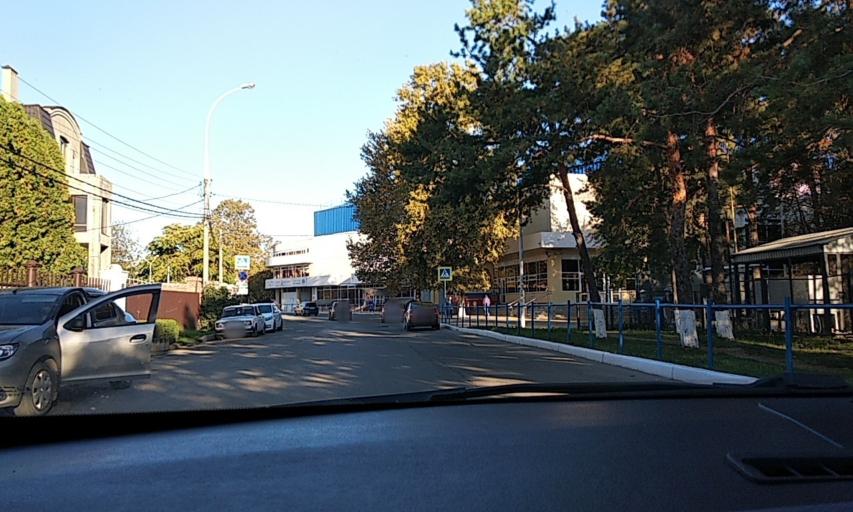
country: RU
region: Adygeya
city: Yablonovskiy
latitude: 45.0156
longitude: 38.9564
